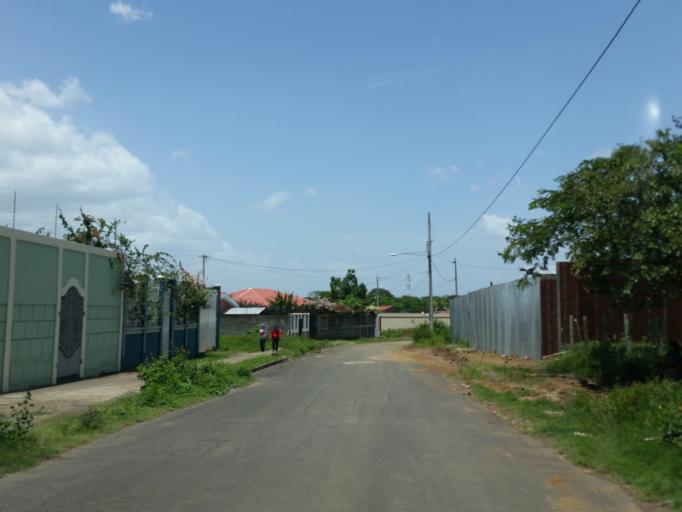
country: NI
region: Managua
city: Managua
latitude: 12.1160
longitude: -86.2717
